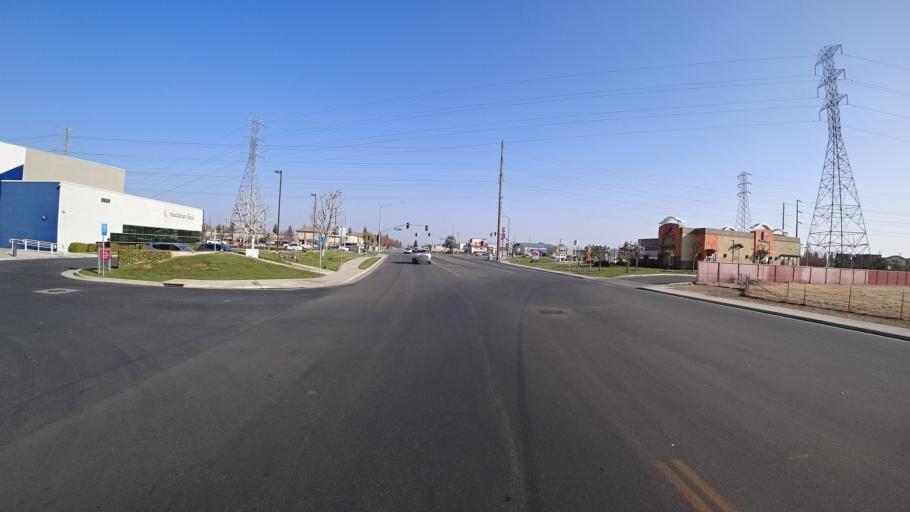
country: US
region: California
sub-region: Kern County
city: Greenacres
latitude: 35.3943
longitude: -119.0933
